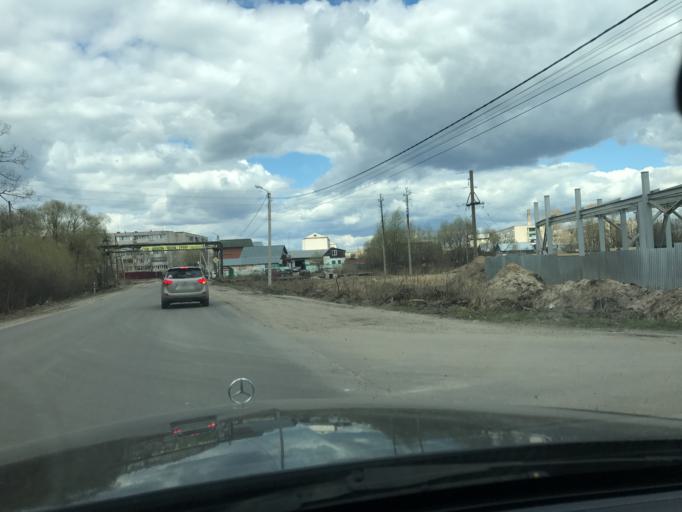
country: RU
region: Vladimir
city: Pokrov
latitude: 55.9095
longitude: 39.1862
